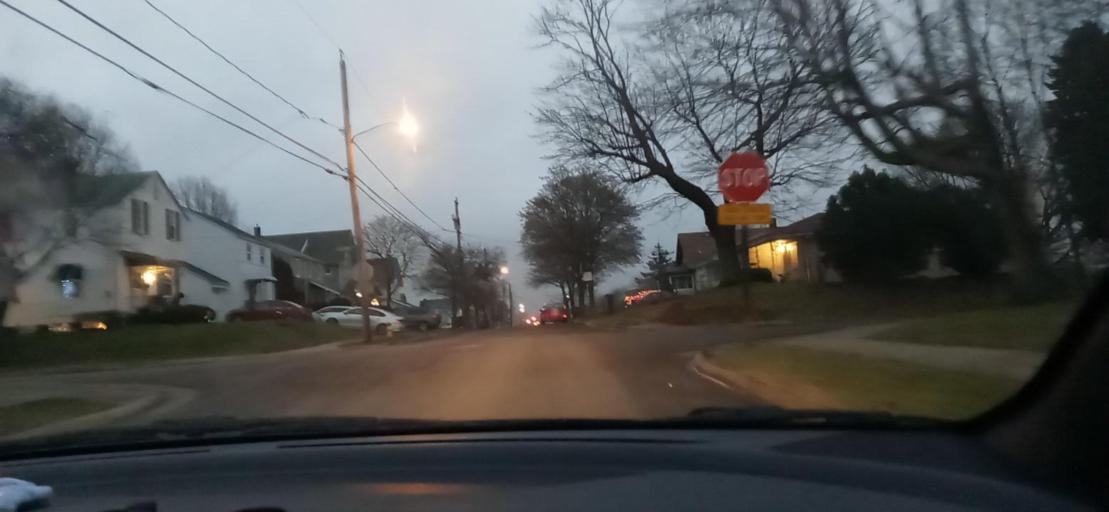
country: US
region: Ohio
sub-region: Summit County
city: Akron
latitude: 41.0414
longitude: -81.4945
